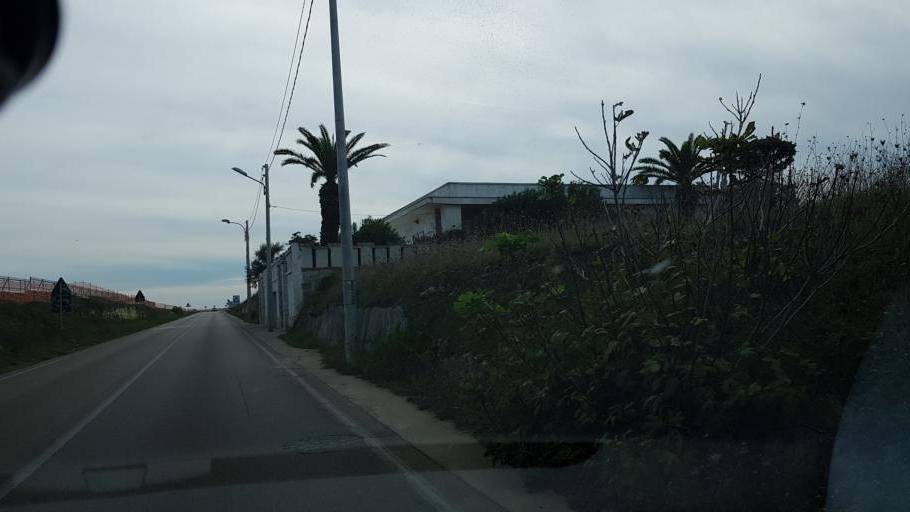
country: IT
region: Apulia
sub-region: Provincia di Lecce
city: Borgagne
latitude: 40.2849
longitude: 18.4273
